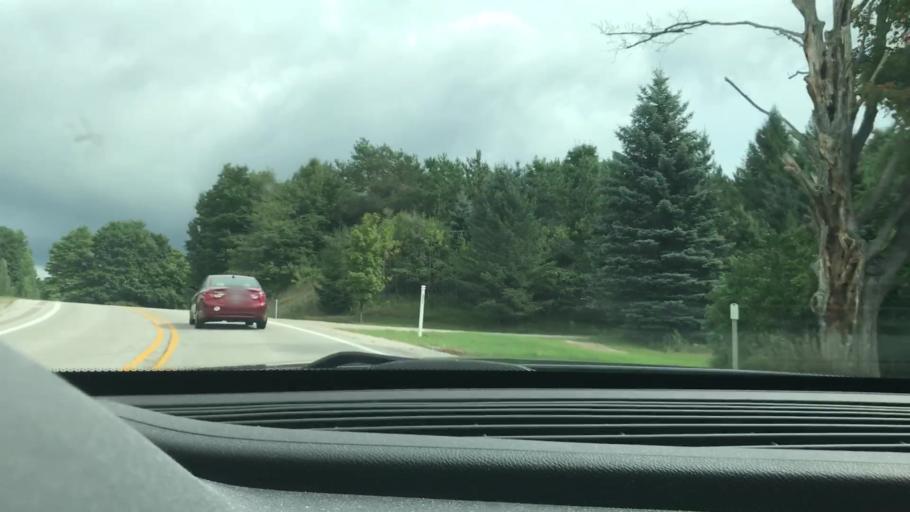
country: US
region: Michigan
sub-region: Antrim County
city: Bellaire
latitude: 45.0849
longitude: -85.2884
